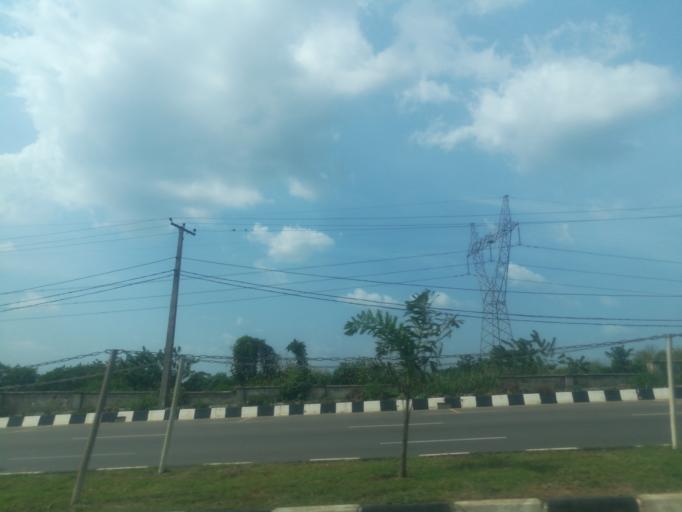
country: NG
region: Ogun
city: Abeokuta
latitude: 7.1301
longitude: 3.3612
